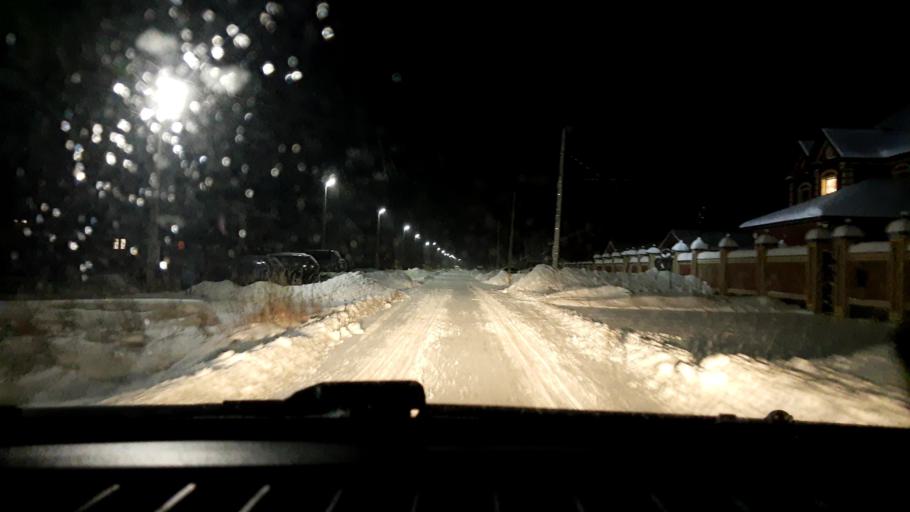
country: RU
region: Nizjnij Novgorod
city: Lukino
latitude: 56.4220
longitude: 43.7171
